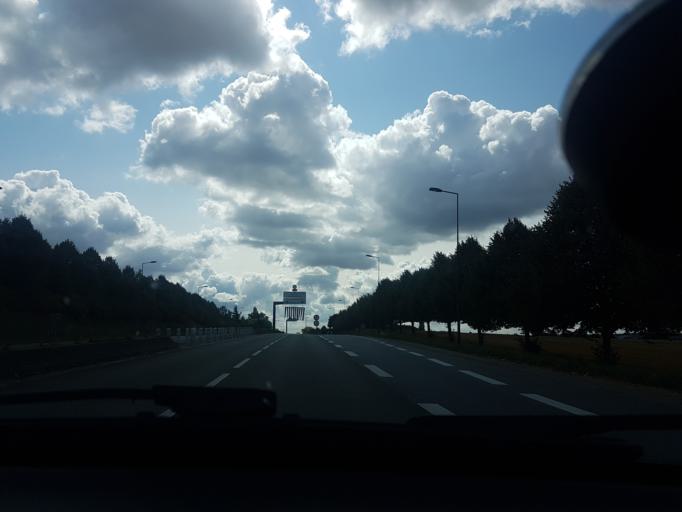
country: FR
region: Ile-de-France
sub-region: Departement des Yvelines
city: Noisy-le-Roi
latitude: 48.8465
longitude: 2.0545
